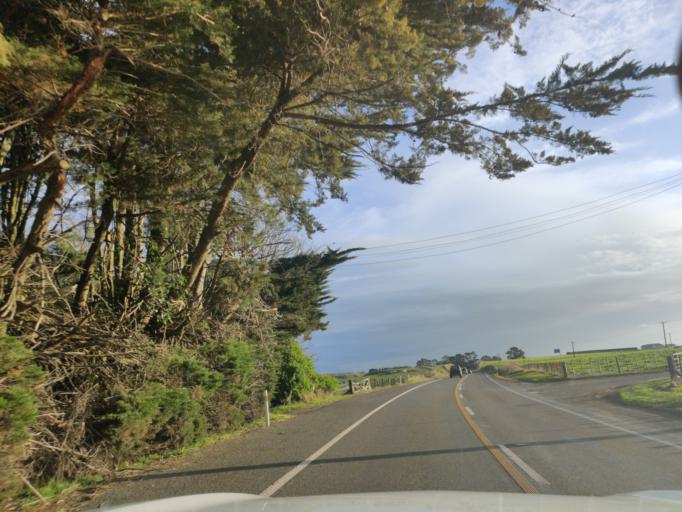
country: NZ
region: Manawatu-Wanganui
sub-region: Horowhenua District
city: Foxton
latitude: -40.5098
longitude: 175.4716
